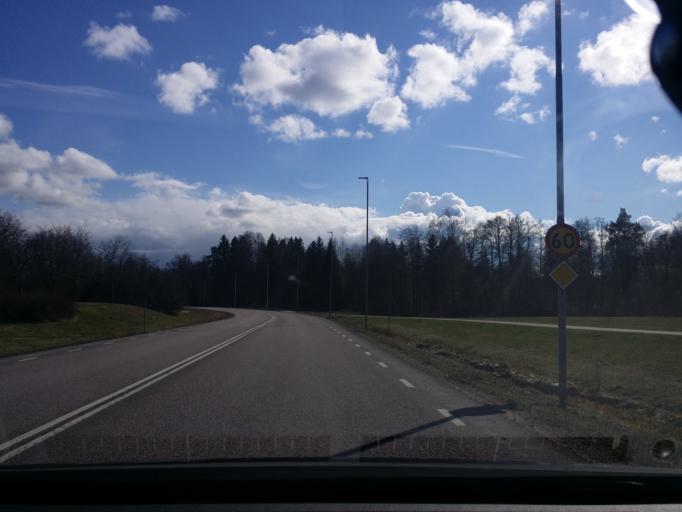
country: SE
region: Vaestmanland
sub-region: Sala Kommun
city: Sala
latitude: 59.9310
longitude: 16.5727
